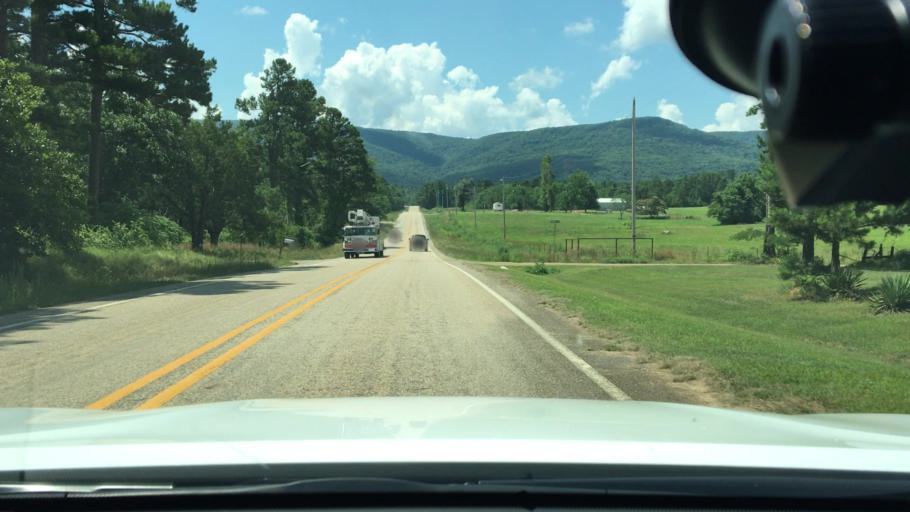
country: US
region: Arkansas
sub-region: Logan County
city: Paris
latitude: 35.2064
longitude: -93.6347
